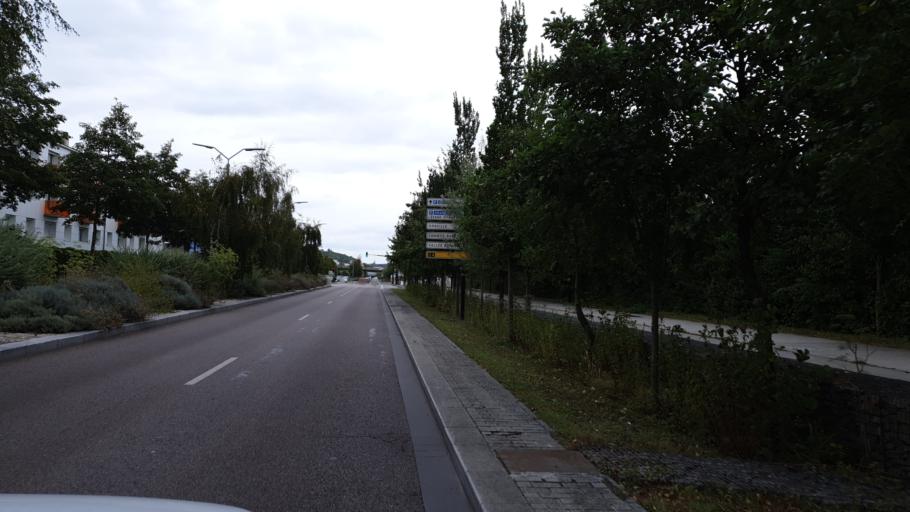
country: FR
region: Haute-Normandie
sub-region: Departement de la Seine-Maritime
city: Fontaine-la-Mallet
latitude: 49.4984
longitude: 0.1570
